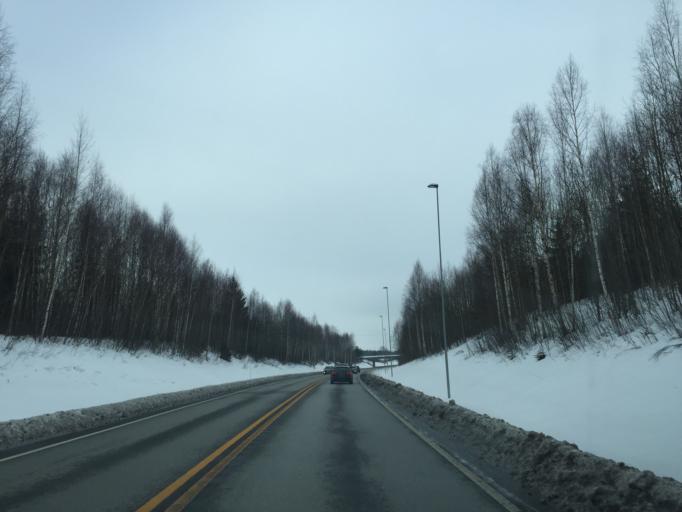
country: NO
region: Hedmark
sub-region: Loten
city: Loten
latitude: 60.7933
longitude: 11.2952
